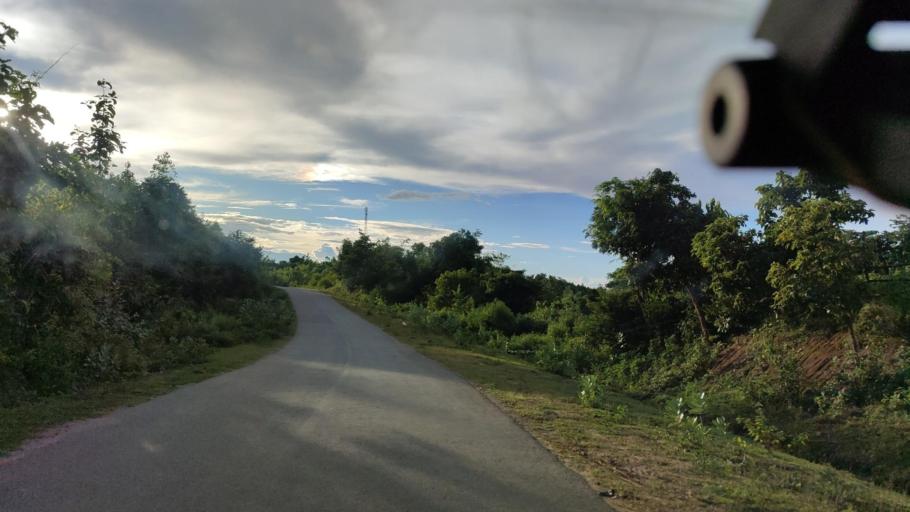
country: MM
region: Magway
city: Taungdwingyi
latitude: 20.0109
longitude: 95.8409
